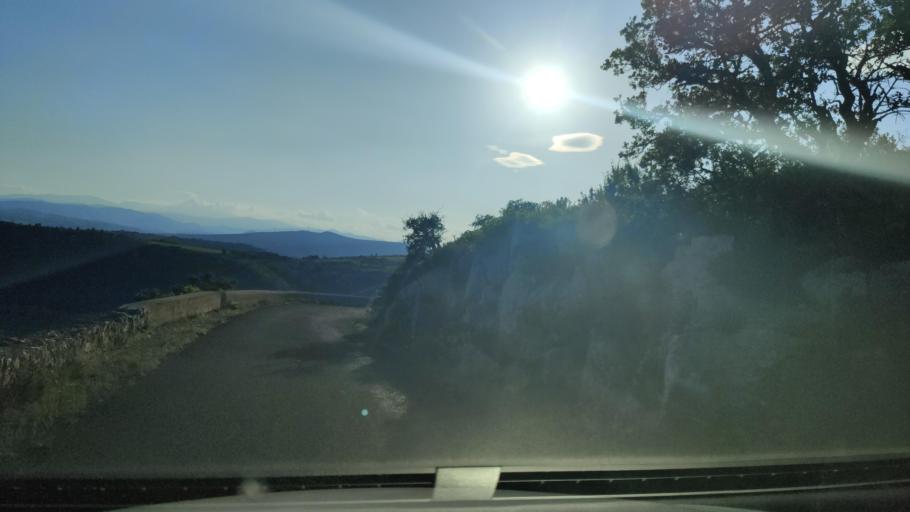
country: FR
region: Languedoc-Roussillon
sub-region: Departement des Pyrenees-Orientales
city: Estagel
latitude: 42.7947
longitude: 2.7252
